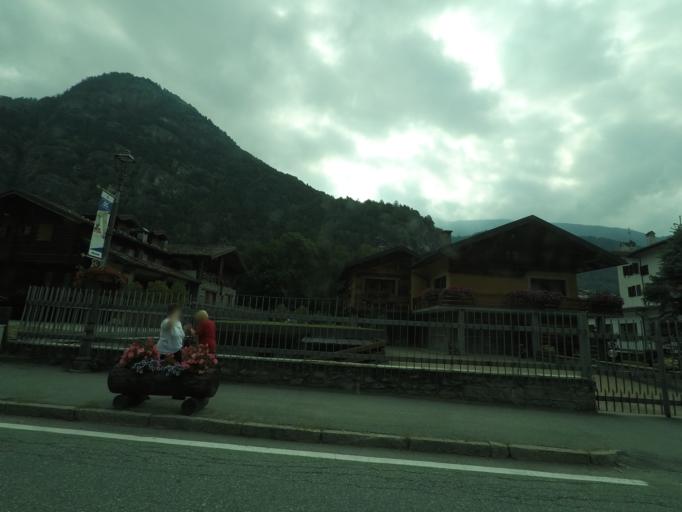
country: IT
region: Aosta Valley
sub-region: Valle d'Aosta
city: Antey-Saint-Andre
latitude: 45.8090
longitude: 7.5875
